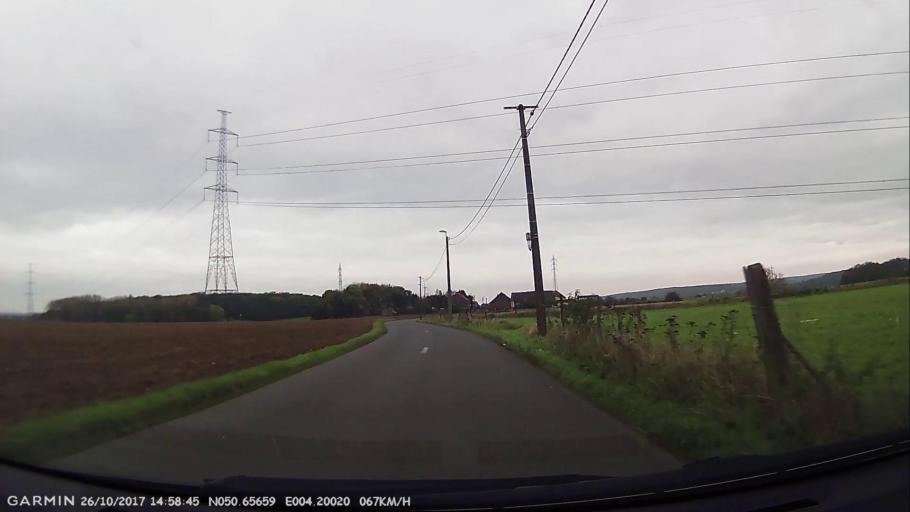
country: BE
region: Wallonia
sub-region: Province du Brabant Wallon
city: Tubize
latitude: 50.6566
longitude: 4.2002
